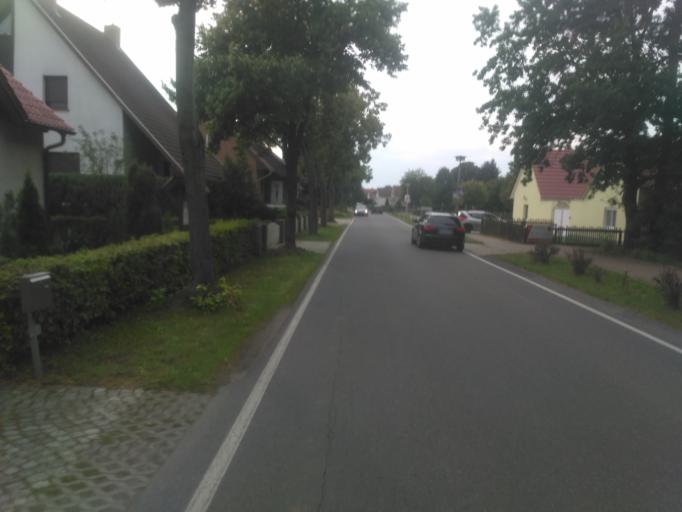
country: DE
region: Brandenburg
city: Welzow
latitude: 51.4936
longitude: 14.1312
